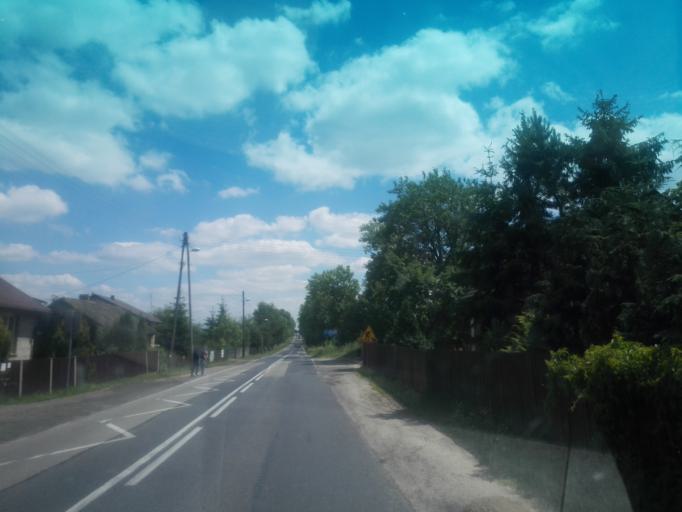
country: PL
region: Silesian Voivodeship
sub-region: Powiat czestochowski
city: Potok Zloty
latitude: 50.7337
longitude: 19.3970
